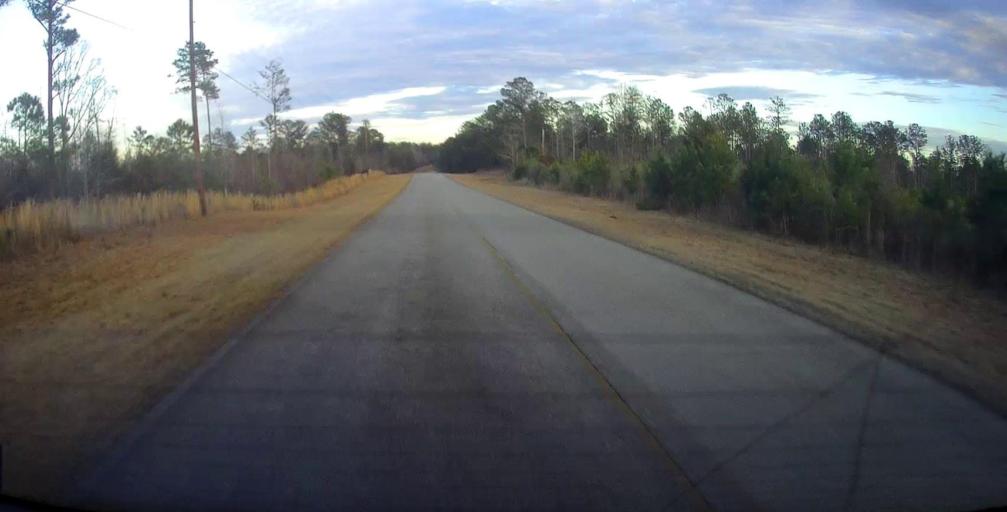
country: US
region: Georgia
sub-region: Harris County
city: Hamilton
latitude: 32.6156
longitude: -84.8291
